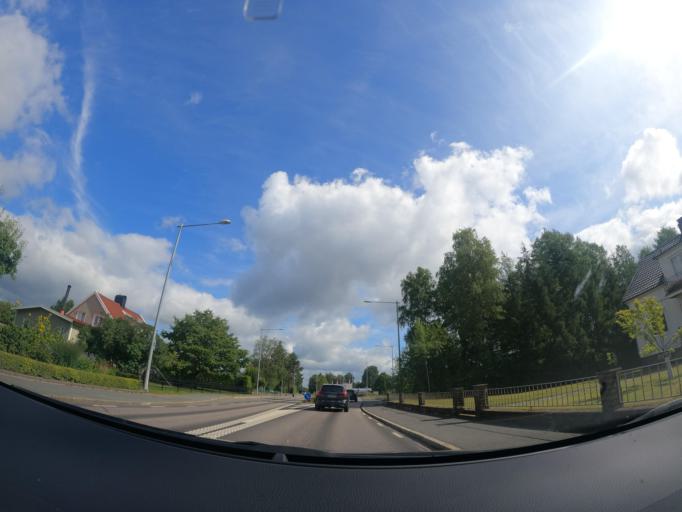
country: SE
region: Joenkoeping
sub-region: Gislaveds Kommun
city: Smalandsstenar
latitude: 57.1519
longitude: 13.3990
